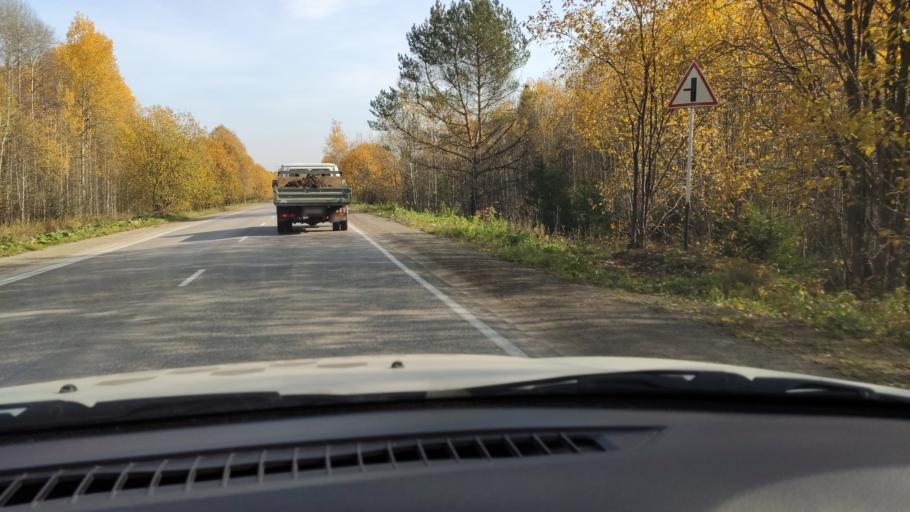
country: RU
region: Perm
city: Novyye Lyady
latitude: 58.0239
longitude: 56.6663
